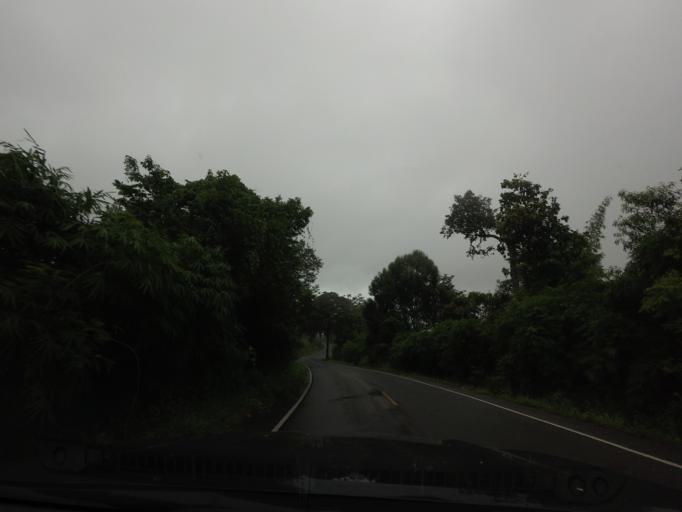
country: TH
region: Nong Khai
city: Sangkhom
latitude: 18.0386
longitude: 102.3274
